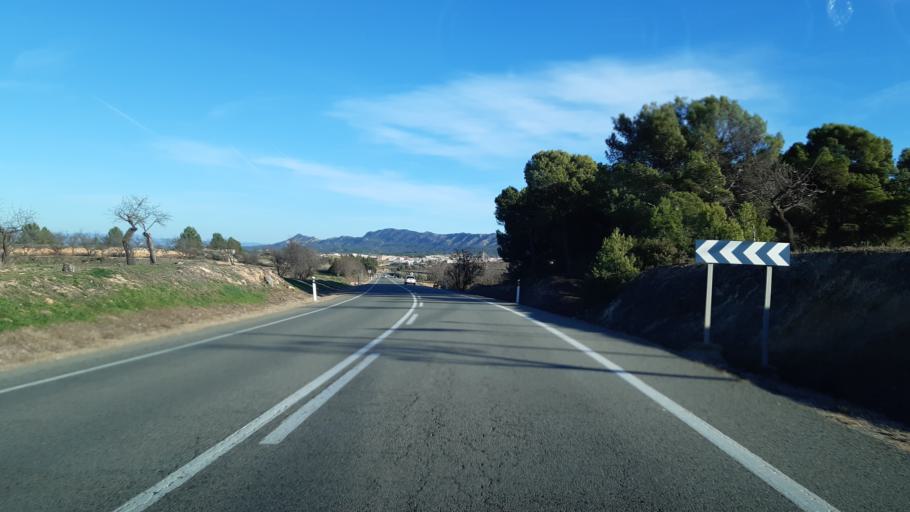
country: ES
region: Catalonia
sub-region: Provincia de Tarragona
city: Gandesa
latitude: 41.0540
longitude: 0.4075
